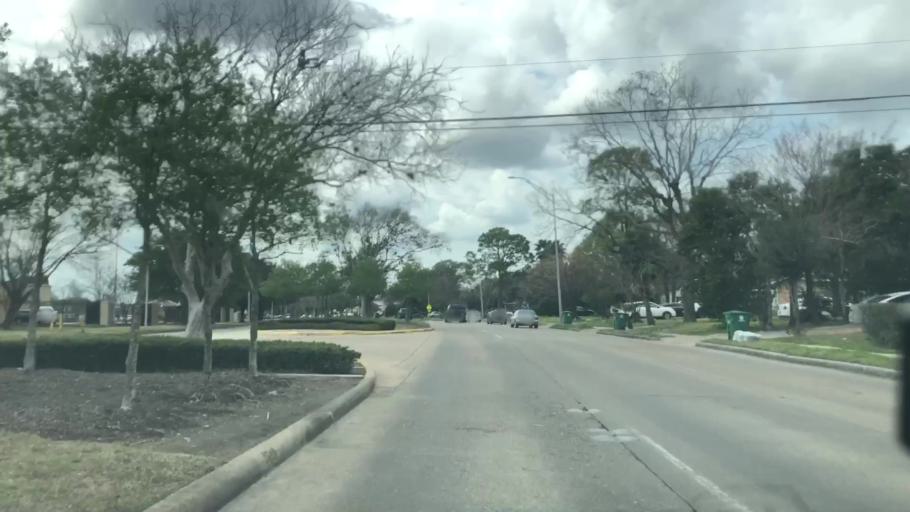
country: US
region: Texas
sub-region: Harris County
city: Bellaire
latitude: 29.6919
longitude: -95.5066
